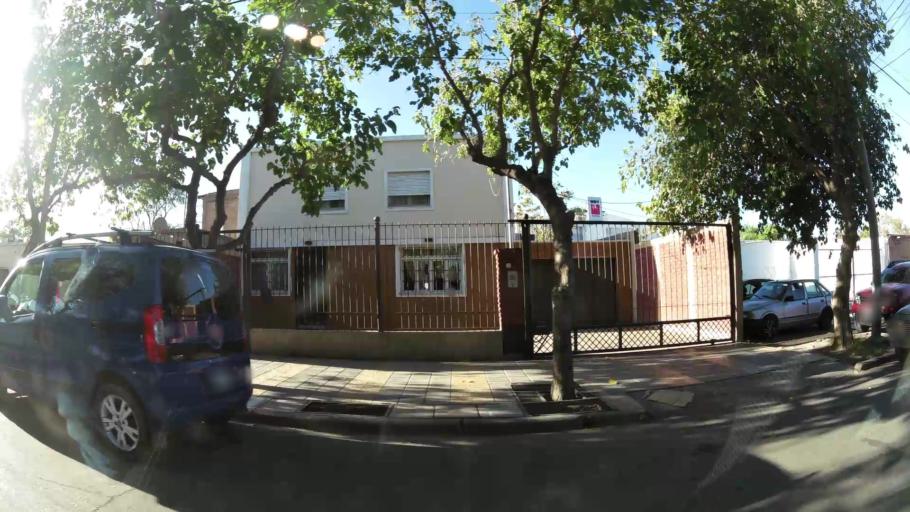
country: AR
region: San Juan
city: Villa Krause
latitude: -31.5522
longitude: -68.5166
